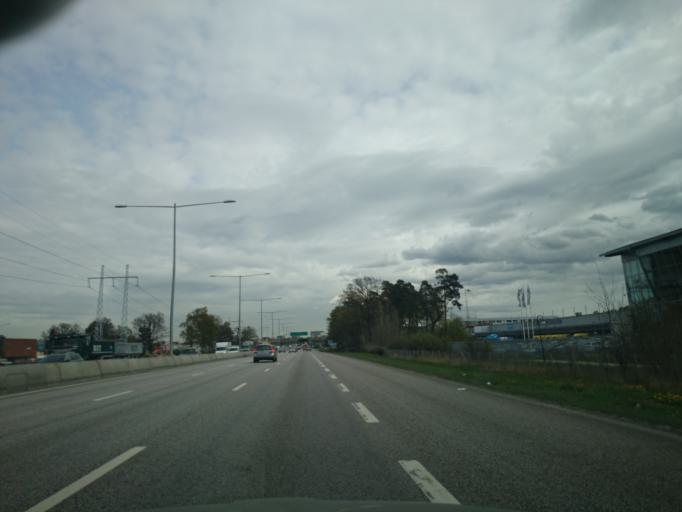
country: SE
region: Stockholm
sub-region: Huddinge Kommun
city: Segeltorp
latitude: 59.2849
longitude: 17.9378
